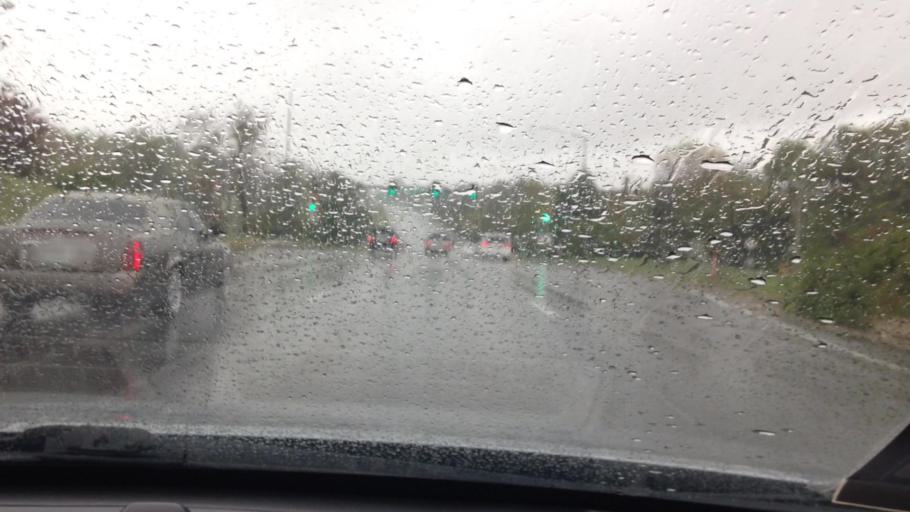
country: US
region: Kansas
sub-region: Johnson County
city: Mission Hills
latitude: 39.0259
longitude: -94.5533
